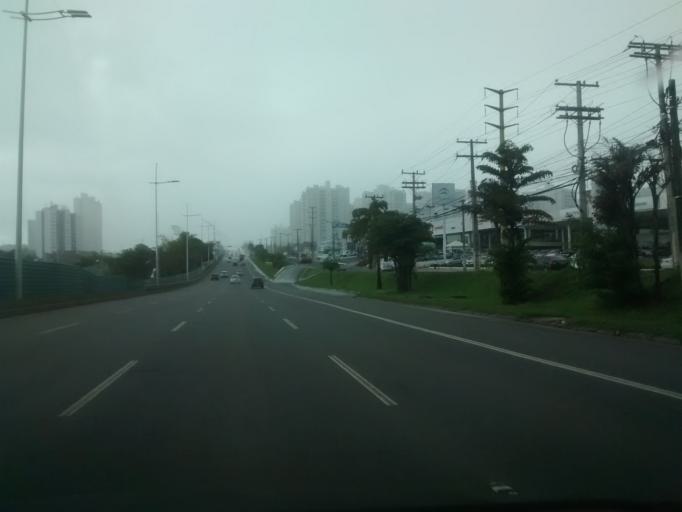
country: BR
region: Bahia
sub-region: Lauro De Freitas
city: Lauro de Freitas
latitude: -12.9394
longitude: -38.4123
